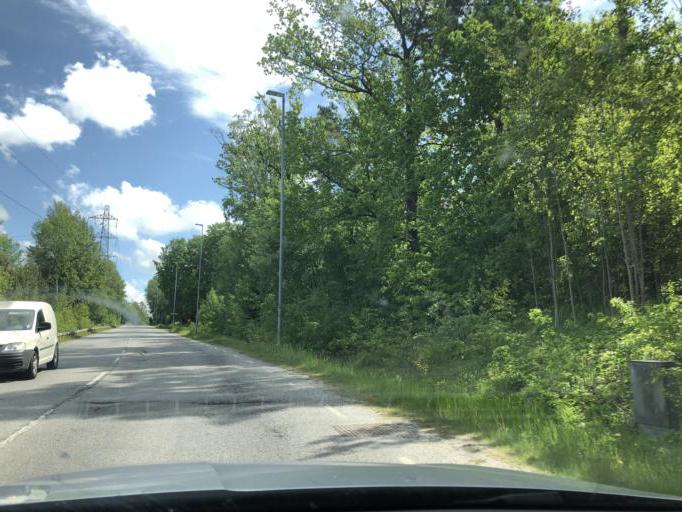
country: SE
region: Stockholm
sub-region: Botkyrka Kommun
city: Alby
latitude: 59.2435
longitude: 17.8430
